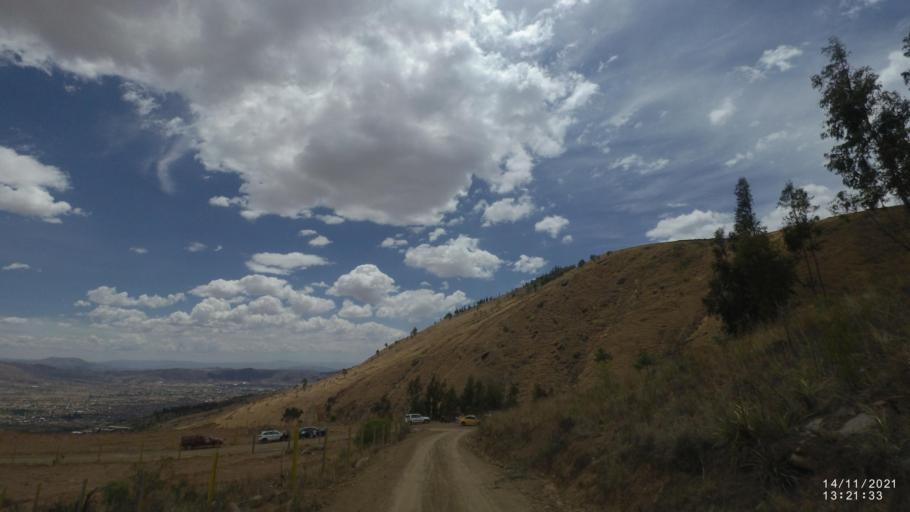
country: BO
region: Cochabamba
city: Colomi
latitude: -17.3754
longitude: -65.9835
